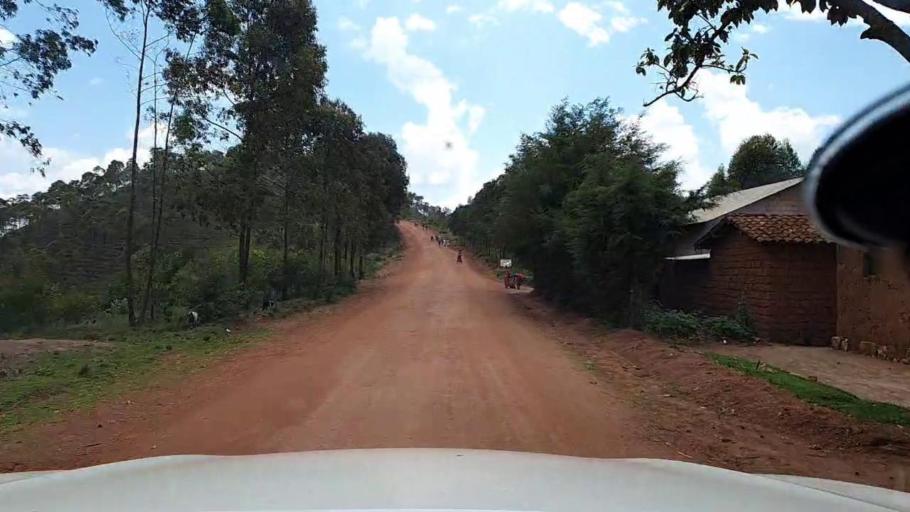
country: RW
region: Kigali
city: Kigali
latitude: -1.7630
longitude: 29.8416
